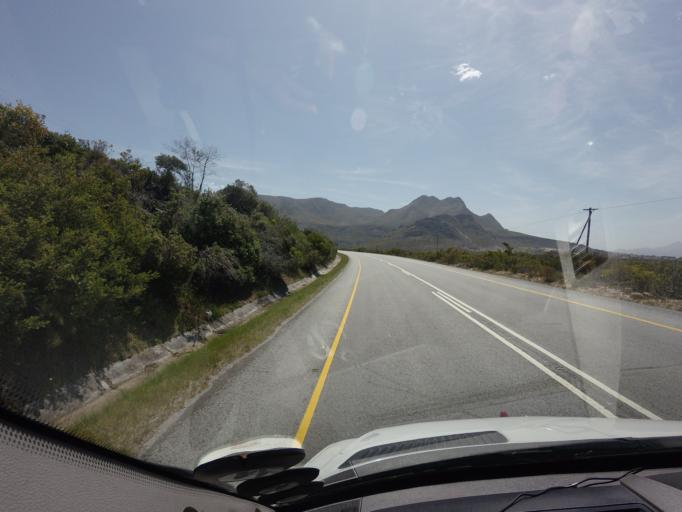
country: ZA
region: Western Cape
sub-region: Overberg District Municipality
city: Grabouw
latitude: -34.3430
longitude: 18.9819
